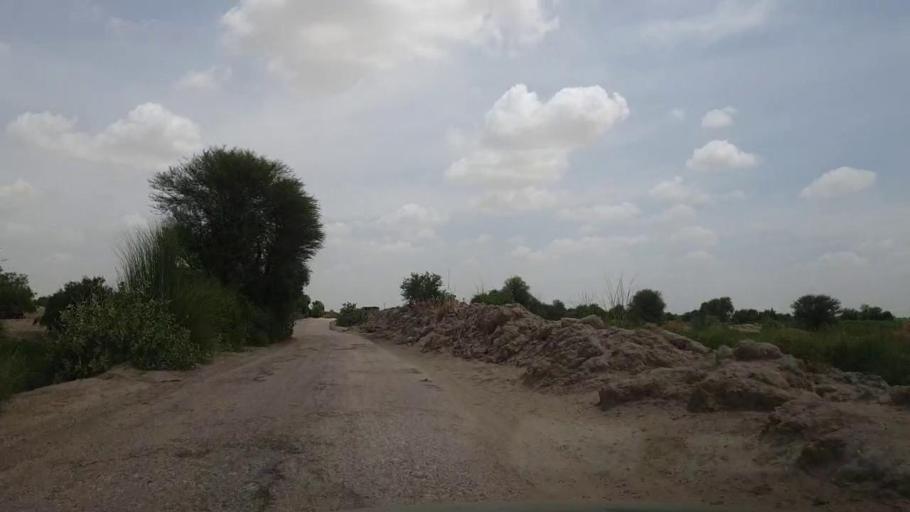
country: PK
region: Sindh
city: Kot Diji
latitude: 27.2141
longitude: 69.1120
